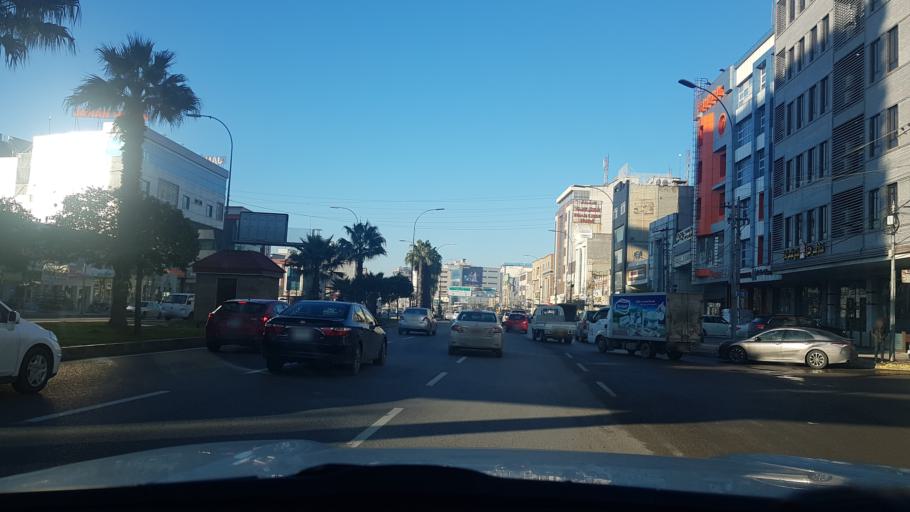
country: IQ
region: Arbil
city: Erbil
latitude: 36.2037
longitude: 44.0085
